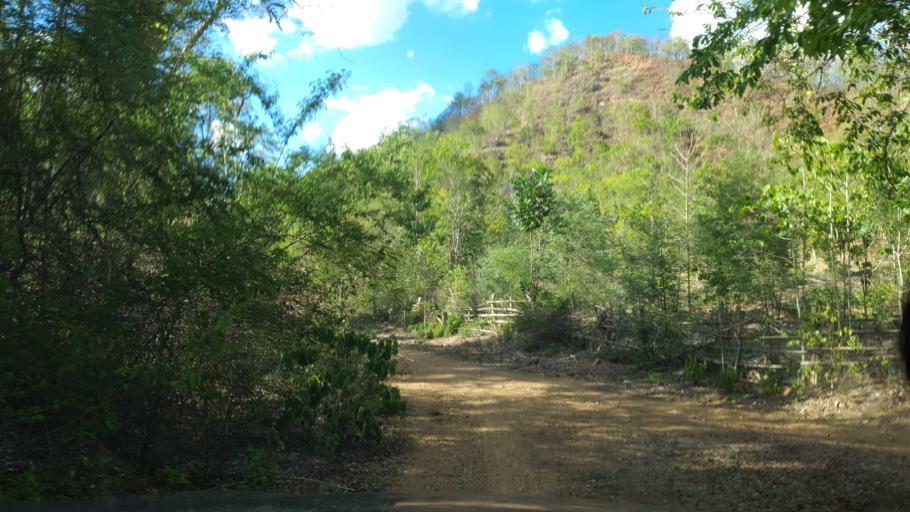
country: TH
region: Lampang
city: Sop Prap
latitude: 17.8416
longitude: 99.2866
